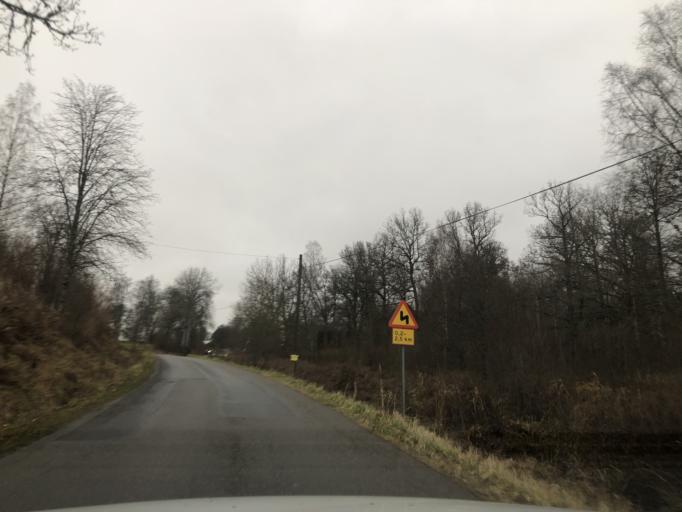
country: SE
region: Vaestra Goetaland
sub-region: Ulricehamns Kommun
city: Ulricehamn
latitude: 57.8879
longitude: 13.4333
